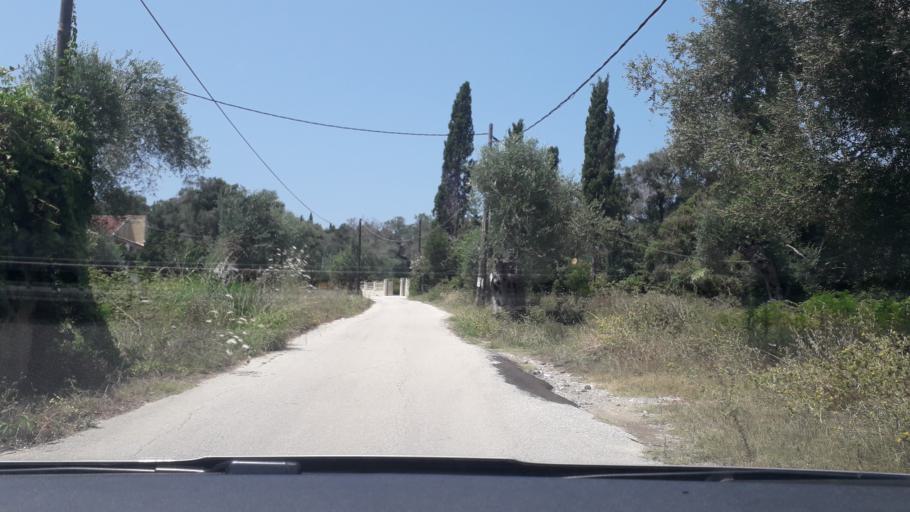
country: GR
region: Ionian Islands
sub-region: Nomos Kerkyras
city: Lefkimmi
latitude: 39.3793
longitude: 20.1115
